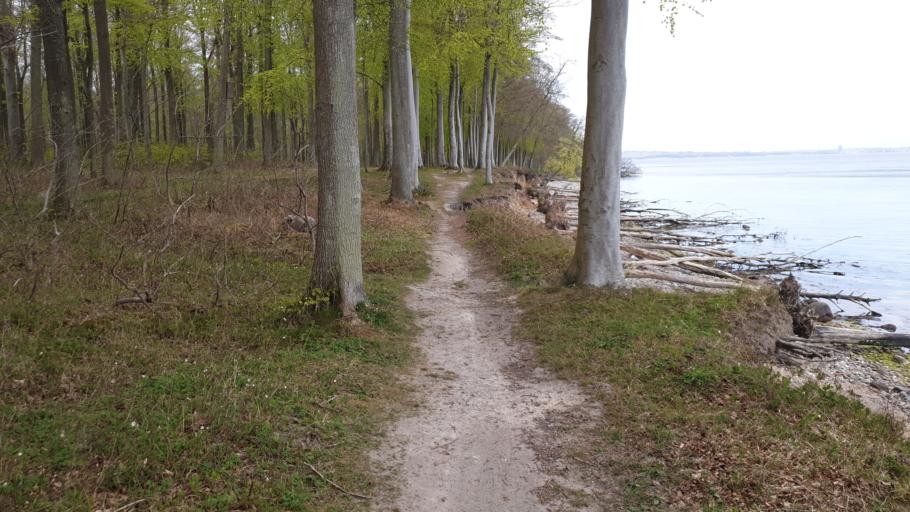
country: DK
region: South Denmark
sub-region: Sonderborg Kommune
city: Dybbol
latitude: 54.8537
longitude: 9.7591
